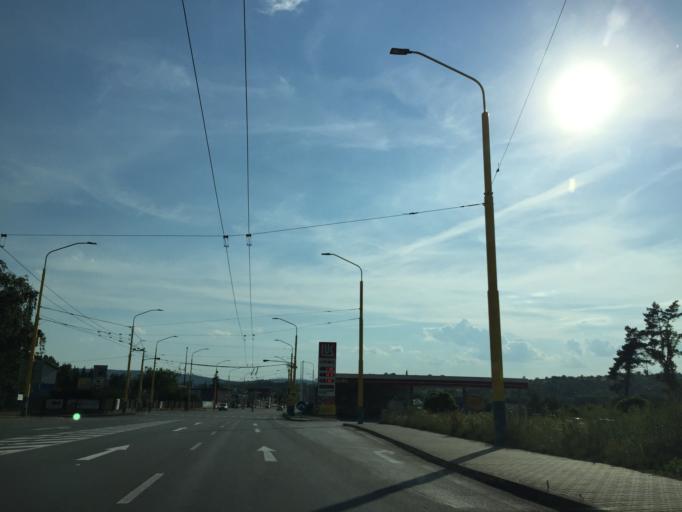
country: SK
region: Presovsky
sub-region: Okres Presov
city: Presov
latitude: 49.0114
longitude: 21.2595
